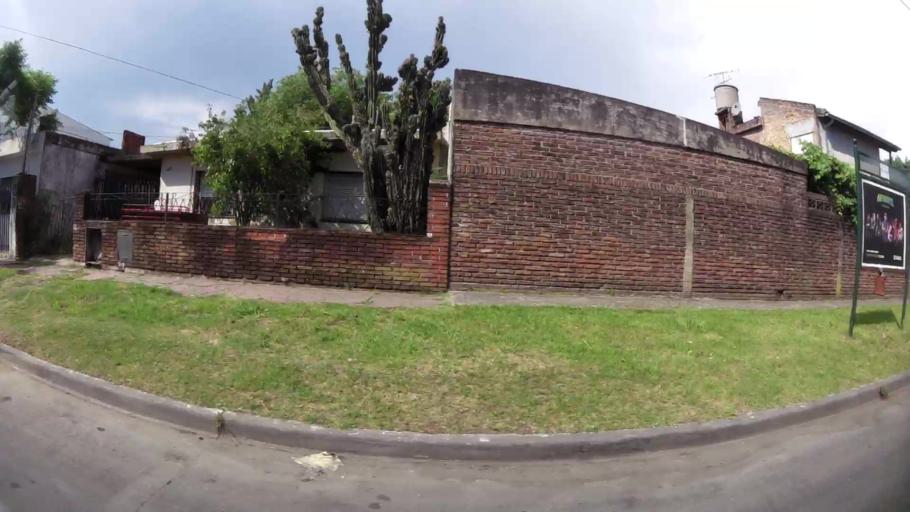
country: AR
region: Buenos Aires
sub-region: Partido de Merlo
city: Merlo
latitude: -34.6390
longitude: -58.6988
